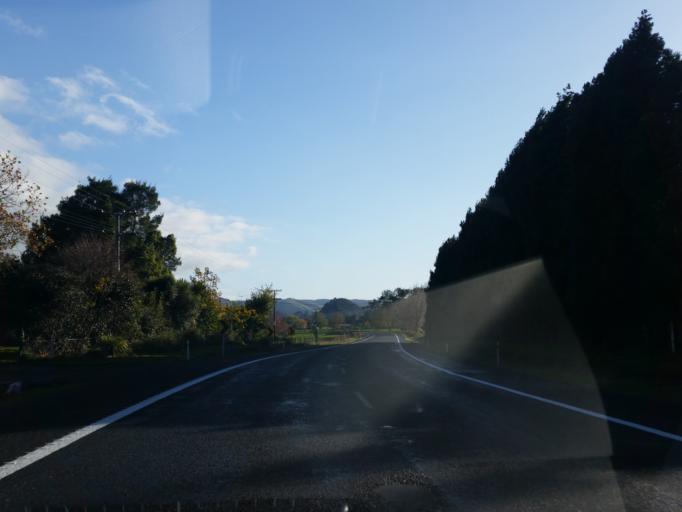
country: NZ
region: Waikato
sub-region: Hauraki District
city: Waihi
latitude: -37.4270
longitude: 175.8703
